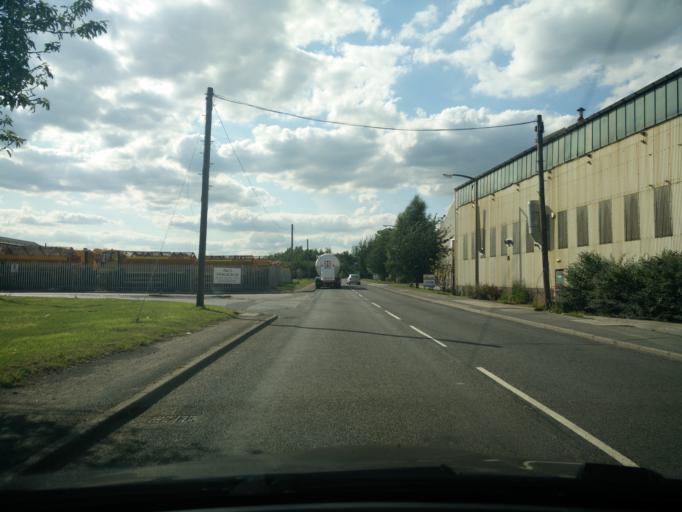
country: GB
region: England
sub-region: Derbyshire
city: Ilkeston
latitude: 52.9446
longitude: -1.2976
